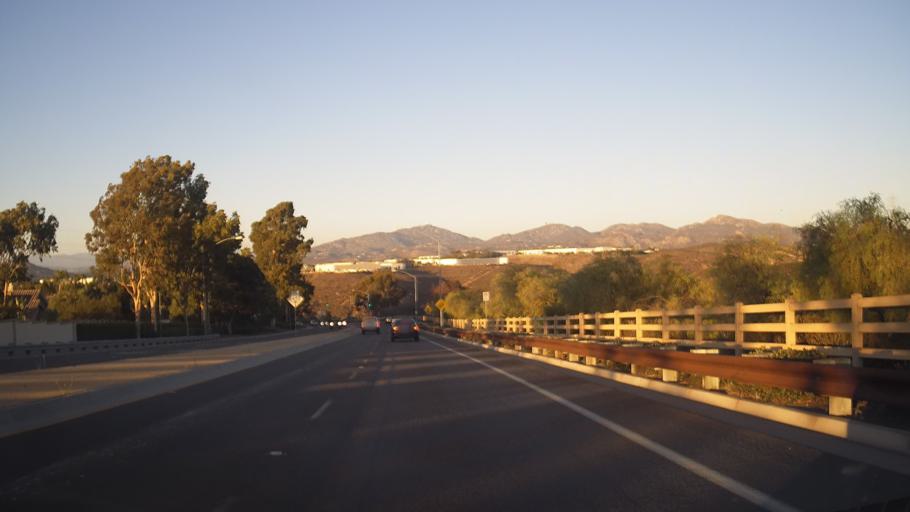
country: US
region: California
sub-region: San Diego County
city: Poway
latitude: 32.9242
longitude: -117.0578
